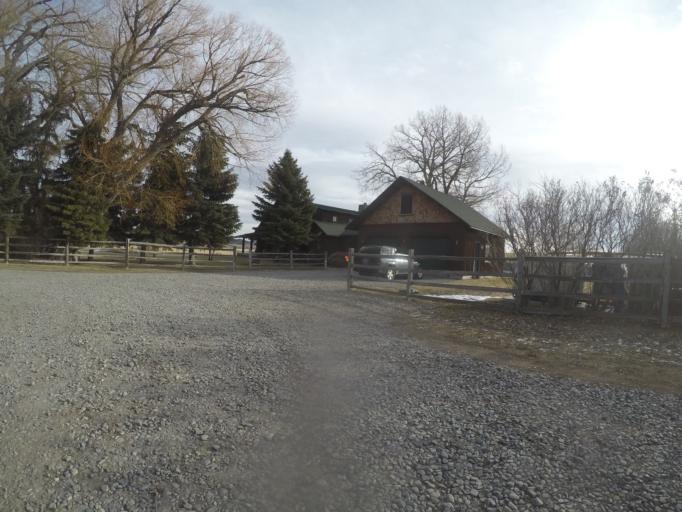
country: US
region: Montana
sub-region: Sweet Grass County
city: Big Timber
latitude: 45.7982
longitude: -109.8668
